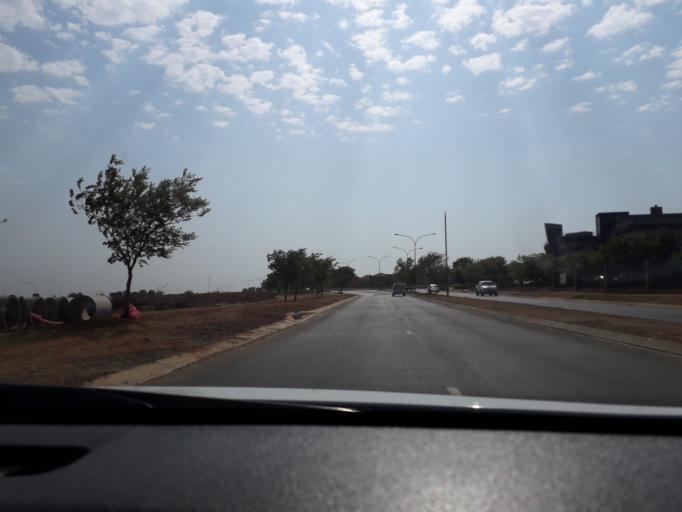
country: ZA
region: Gauteng
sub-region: Ekurhuleni Metropolitan Municipality
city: Tembisa
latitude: -26.0738
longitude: 28.2594
